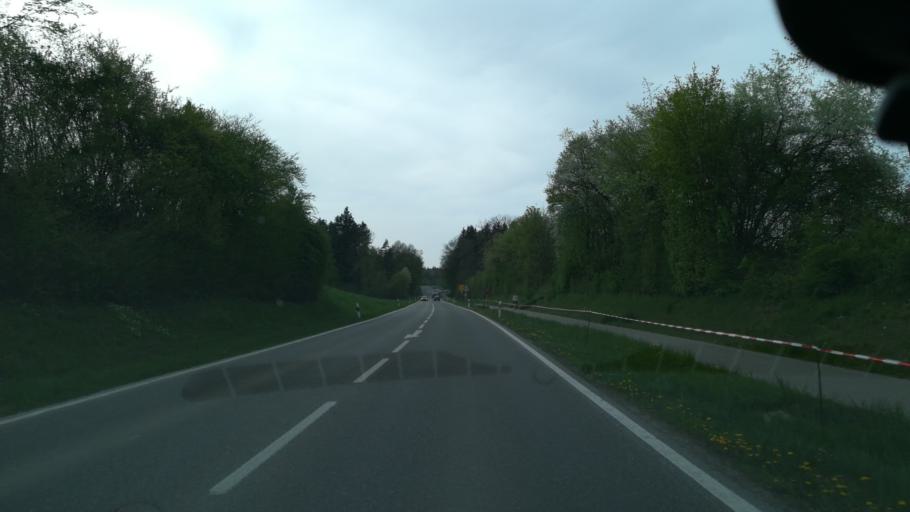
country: DE
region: Baden-Wuerttemberg
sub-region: Freiburg Region
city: Moos
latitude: 47.7562
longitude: 8.9120
